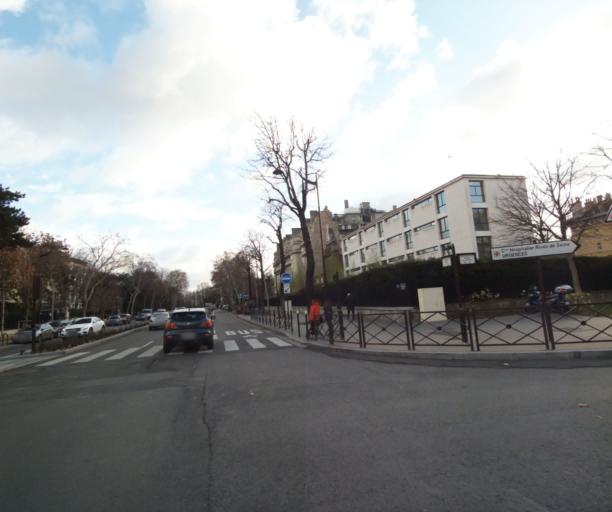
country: FR
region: Ile-de-France
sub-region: Departement des Hauts-de-Seine
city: Neuilly-sur-Seine
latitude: 48.8923
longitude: 2.2688
